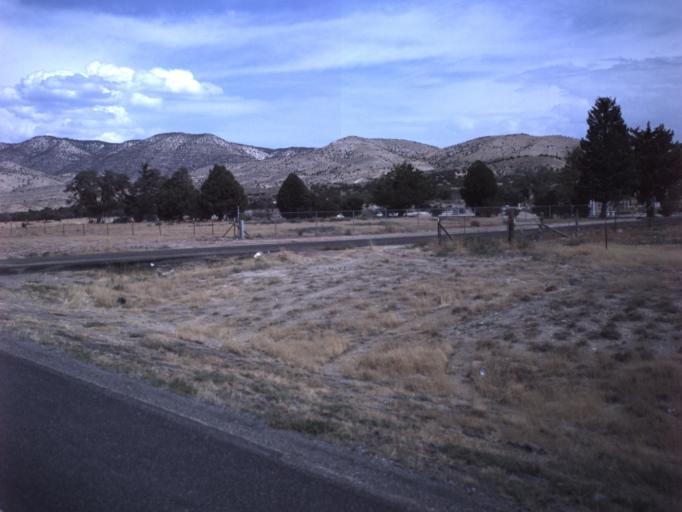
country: US
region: Utah
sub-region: Sanpete County
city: Gunnison
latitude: 39.2225
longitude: -111.8481
